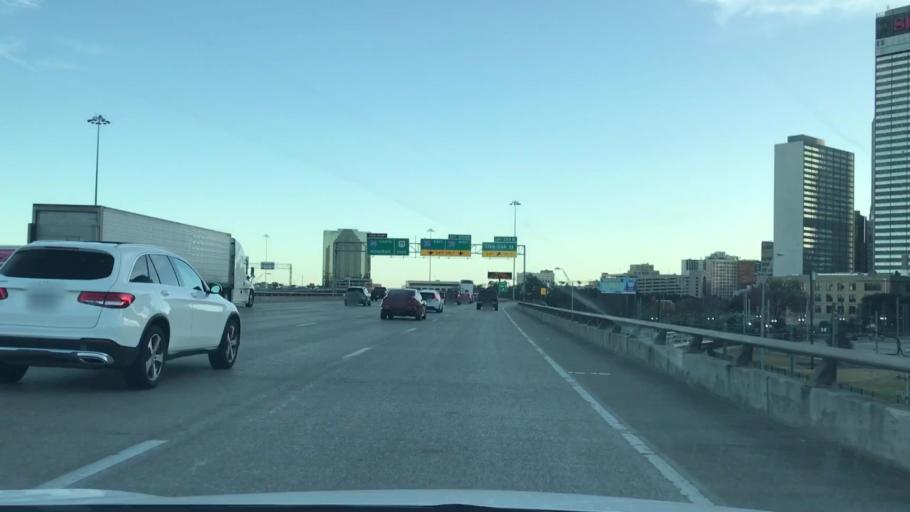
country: US
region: Texas
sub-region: Dallas County
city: Dallas
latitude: 32.7895
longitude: -96.7926
